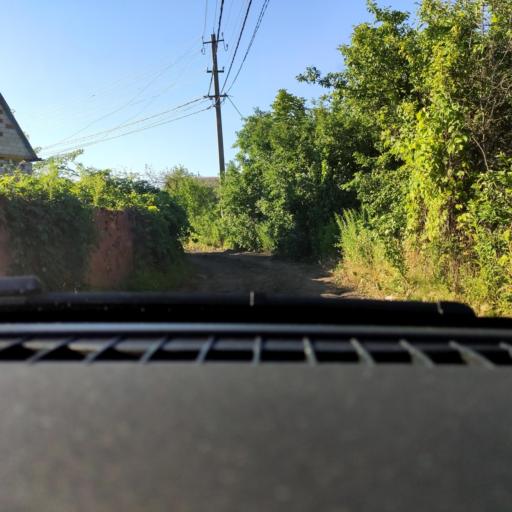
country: RU
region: Voronezj
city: Maslovka
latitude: 51.5163
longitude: 39.2197
